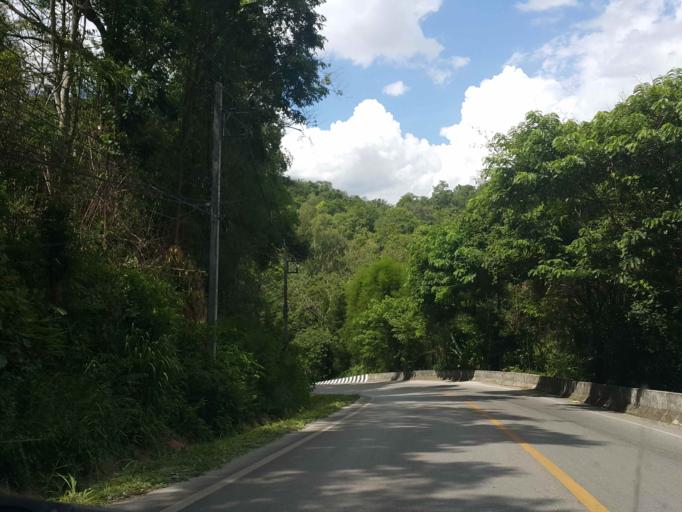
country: TH
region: Chiang Mai
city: Samoeng
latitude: 18.8978
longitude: 98.8469
